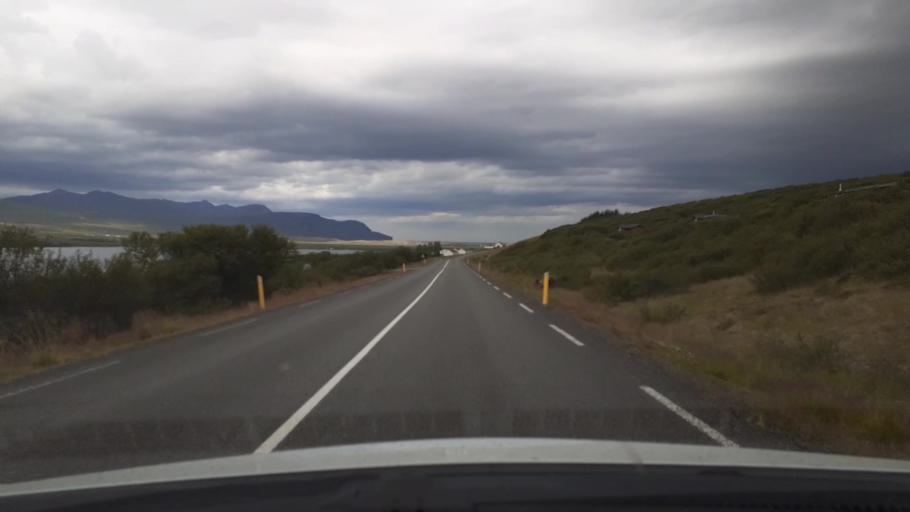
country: IS
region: West
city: Borgarnes
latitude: 64.5430
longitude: -21.5639
